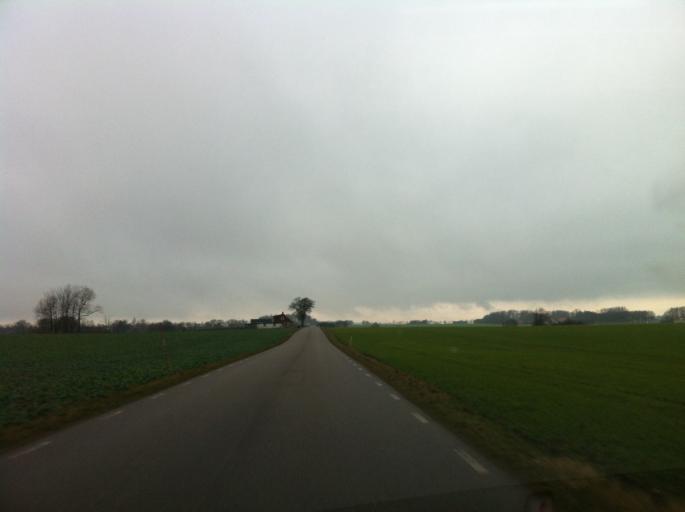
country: SE
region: Skane
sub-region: Helsingborg
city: Barslov
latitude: 55.9764
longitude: 12.8702
